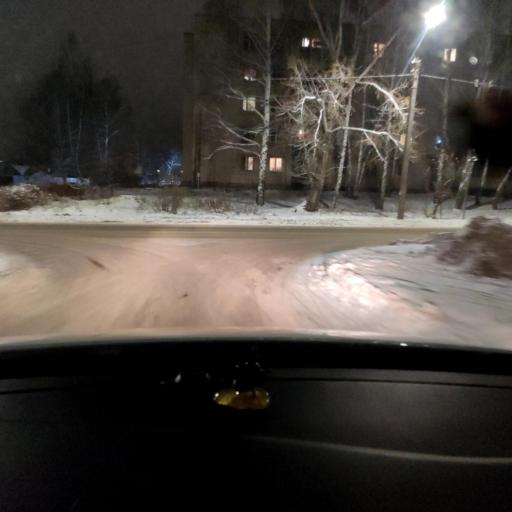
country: RU
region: Tatarstan
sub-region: Zelenodol'skiy Rayon
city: Zelenodolsk
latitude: 55.8507
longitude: 48.5577
